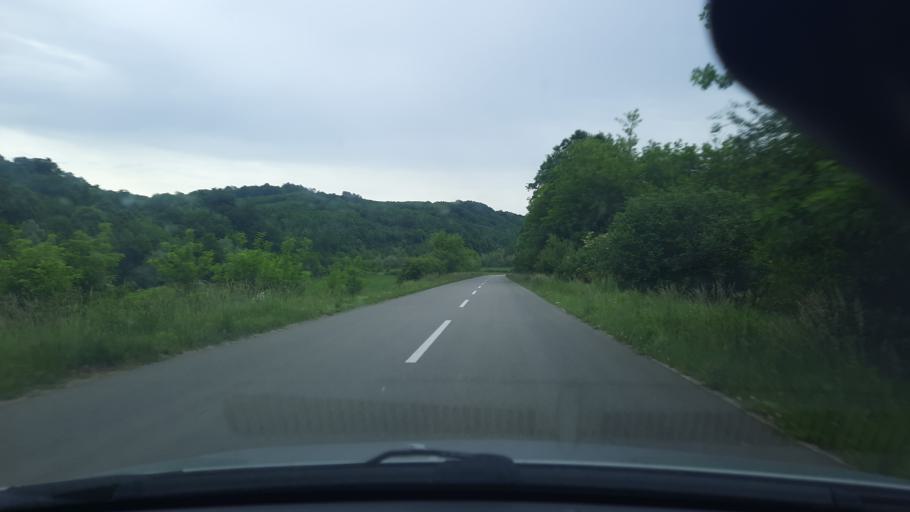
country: RS
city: Bukor
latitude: 44.5308
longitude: 19.5141
